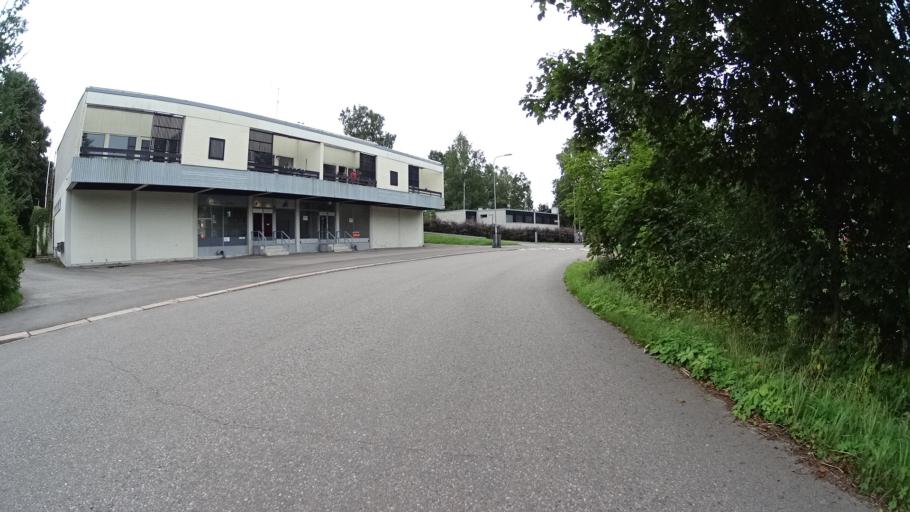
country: FI
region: Uusimaa
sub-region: Helsinki
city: Helsinki
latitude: 60.2236
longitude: 24.9387
